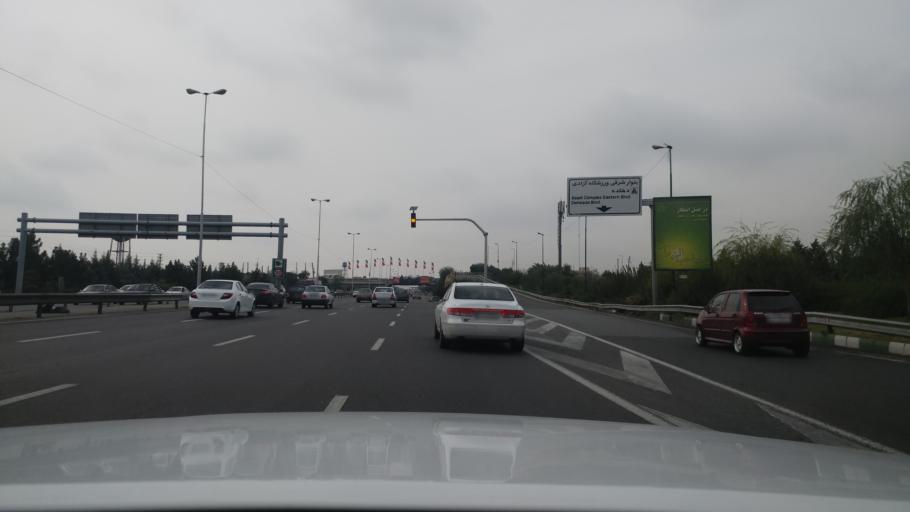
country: IR
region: Tehran
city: Tehran
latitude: 35.7164
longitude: 51.2903
